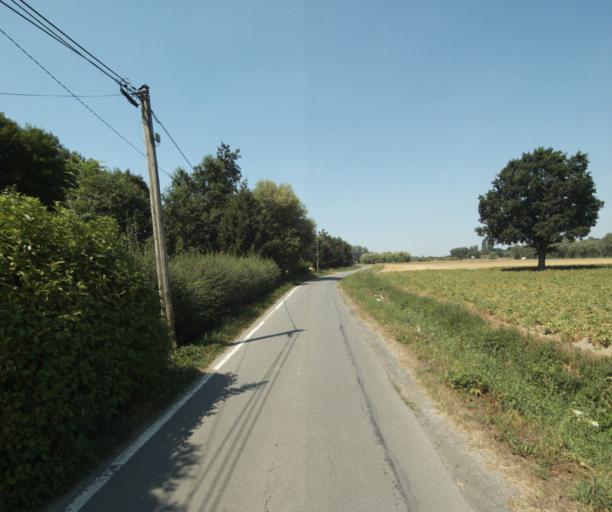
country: FR
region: Nord-Pas-de-Calais
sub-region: Departement du Nord
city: Comines
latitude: 50.7508
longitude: 3.0286
